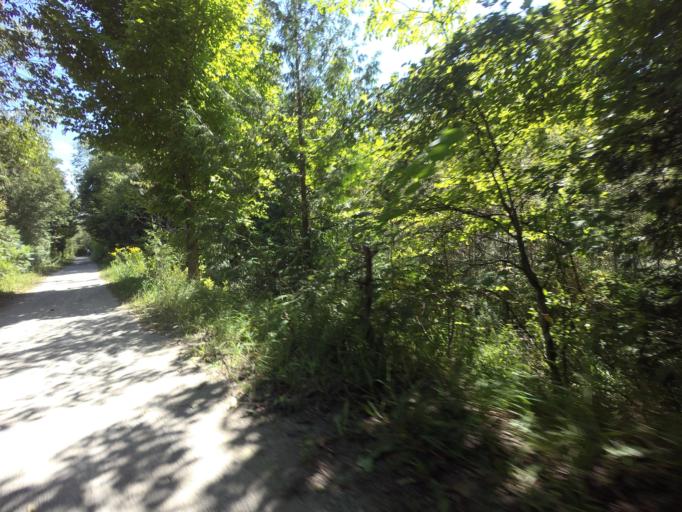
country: CA
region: Ontario
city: Orangeville
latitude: 43.7748
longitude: -80.1007
